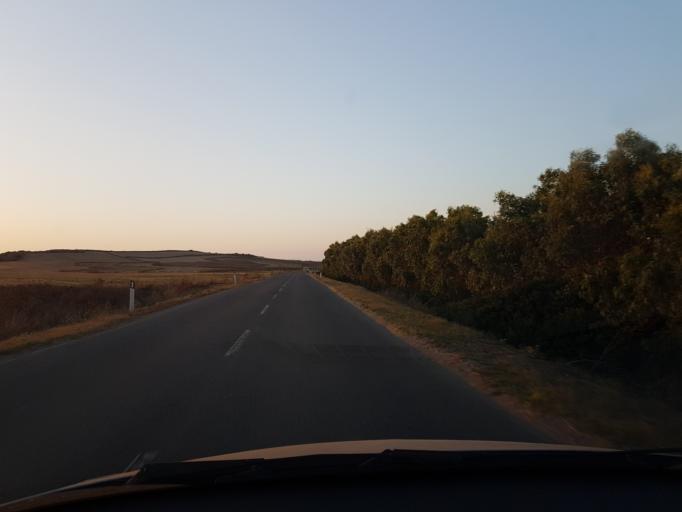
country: IT
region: Sardinia
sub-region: Provincia di Oristano
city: Nurachi
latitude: 39.9722
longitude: 8.4527
